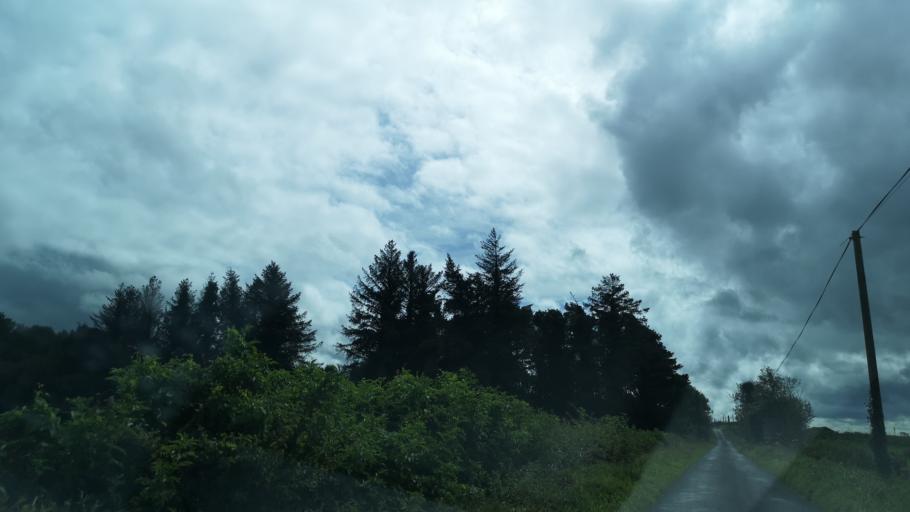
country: IE
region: Connaught
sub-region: County Galway
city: Athenry
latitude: 53.2866
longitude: -8.6658
